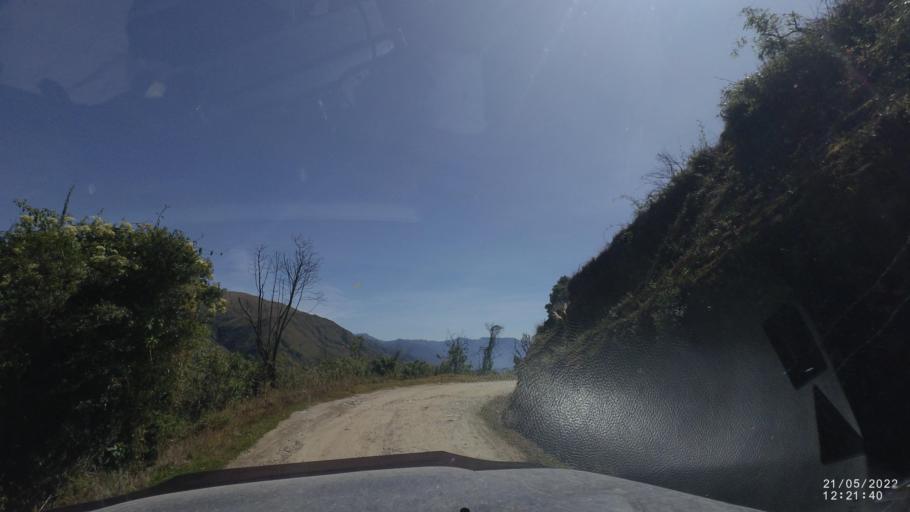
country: BO
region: Cochabamba
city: Colomi
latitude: -17.2244
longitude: -65.9038
